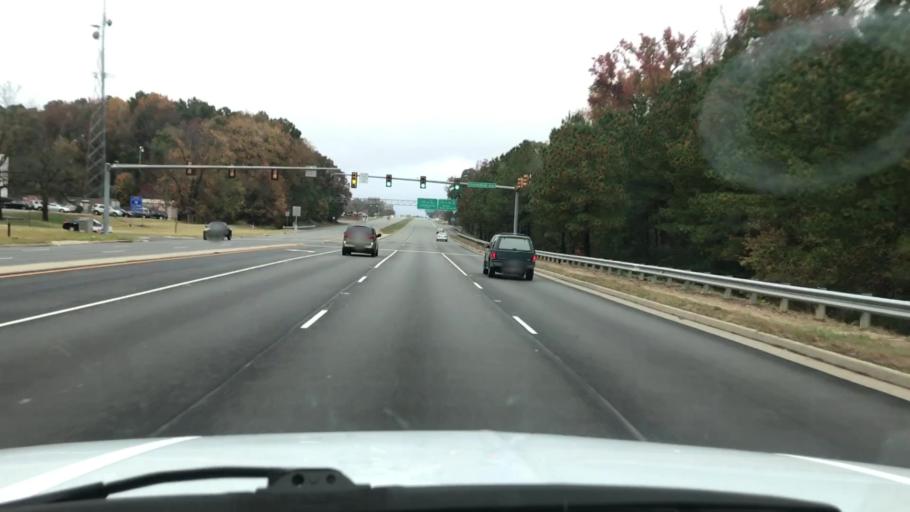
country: US
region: Virginia
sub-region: Henrico County
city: Chamberlayne
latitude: 37.6523
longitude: -77.4597
